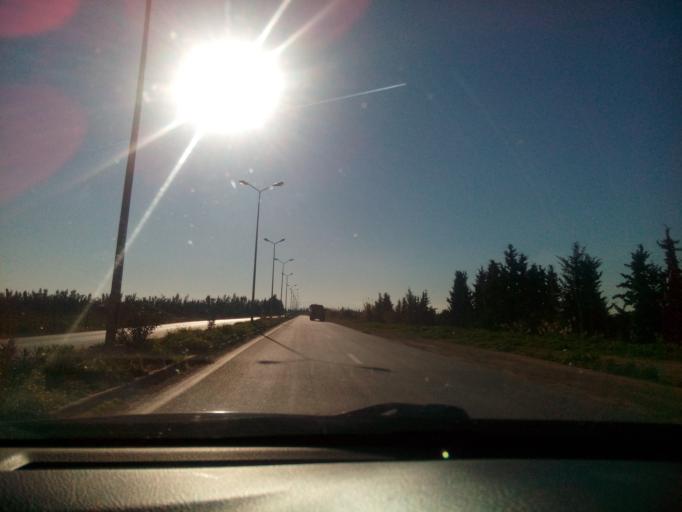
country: DZ
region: Relizane
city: Relizane
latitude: 35.7385
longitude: 0.6038
